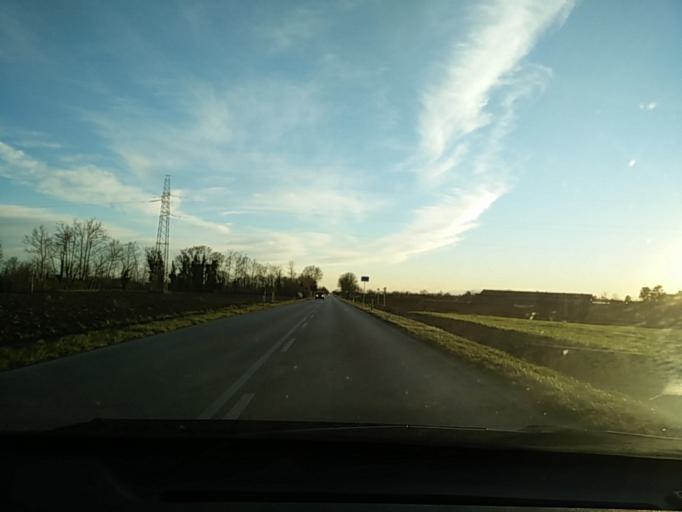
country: IT
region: Friuli Venezia Giulia
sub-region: Provincia di Udine
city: Talmassons
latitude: 45.9612
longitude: 13.1036
